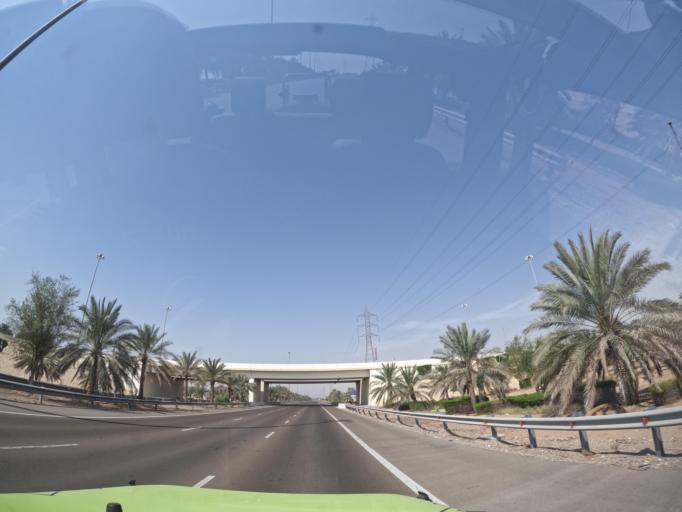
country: AE
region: Abu Dhabi
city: Al Ain
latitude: 24.2111
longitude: 55.4657
